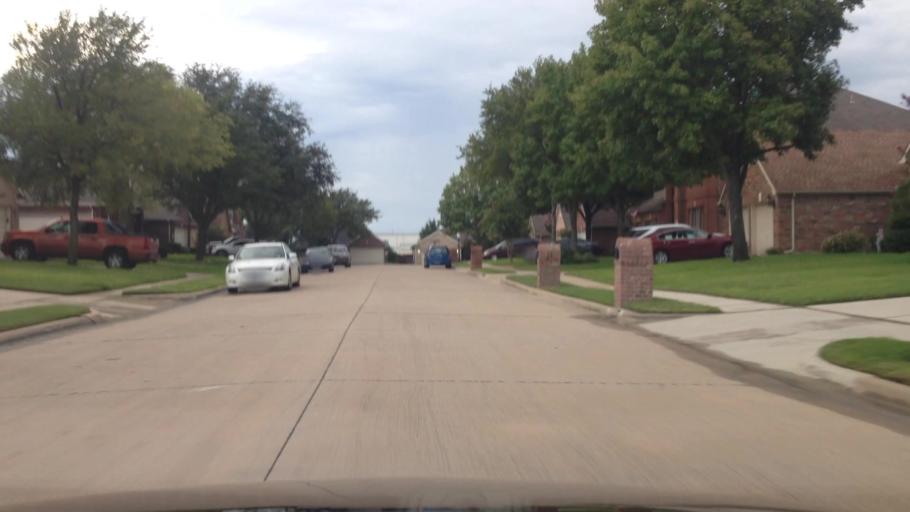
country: US
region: Texas
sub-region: Denton County
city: Flower Mound
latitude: 33.0018
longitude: -97.0562
